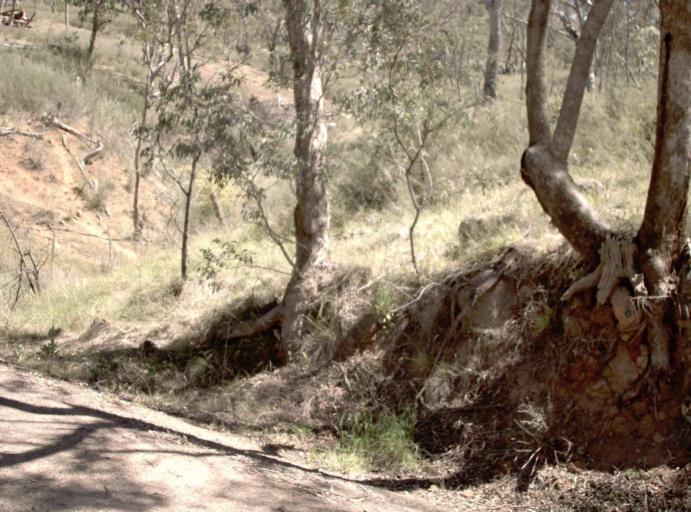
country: AU
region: New South Wales
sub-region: Snowy River
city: Jindabyne
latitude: -37.0623
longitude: 148.5749
